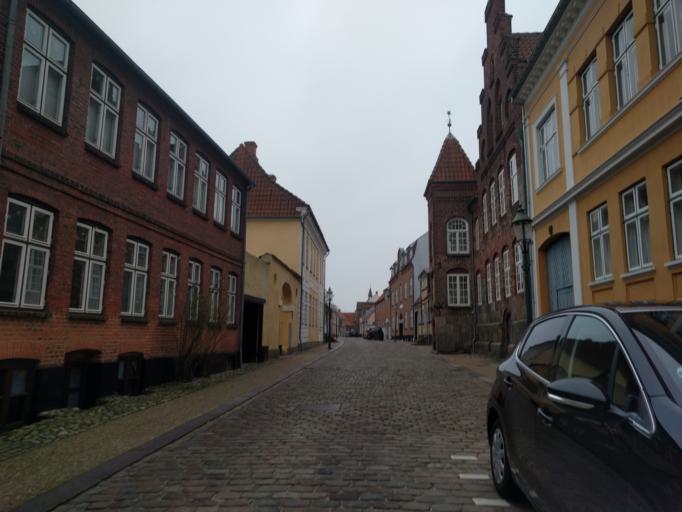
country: DK
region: Central Jutland
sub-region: Viborg Kommune
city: Viborg
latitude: 56.4535
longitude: 9.4121
